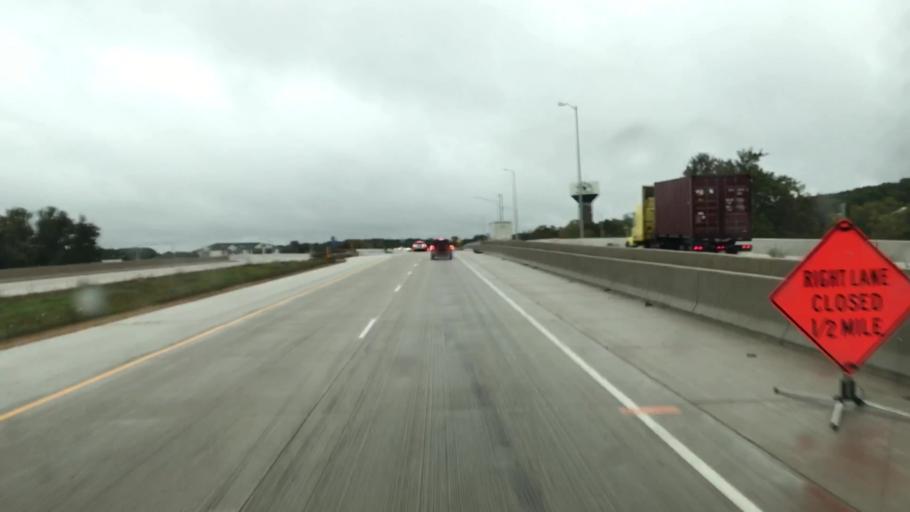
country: US
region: Wisconsin
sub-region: Waukesha County
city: New Berlin
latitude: 42.9514
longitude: -88.1104
